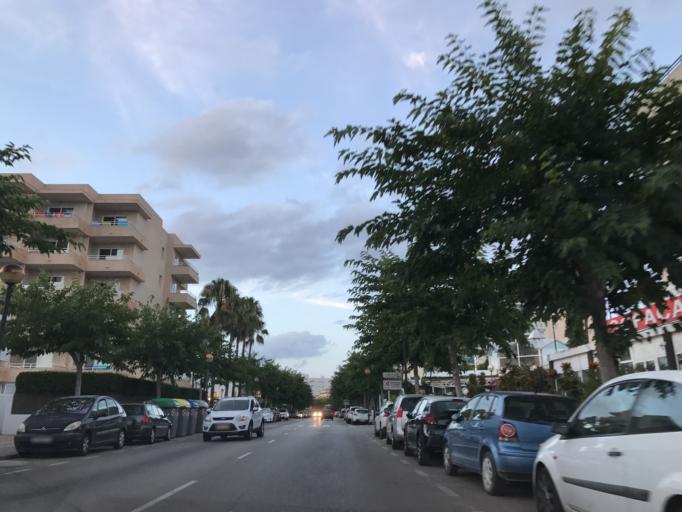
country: ES
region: Balearic Islands
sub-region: Illes Balears
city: Son Servera
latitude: 39.5961
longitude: 3.3796
